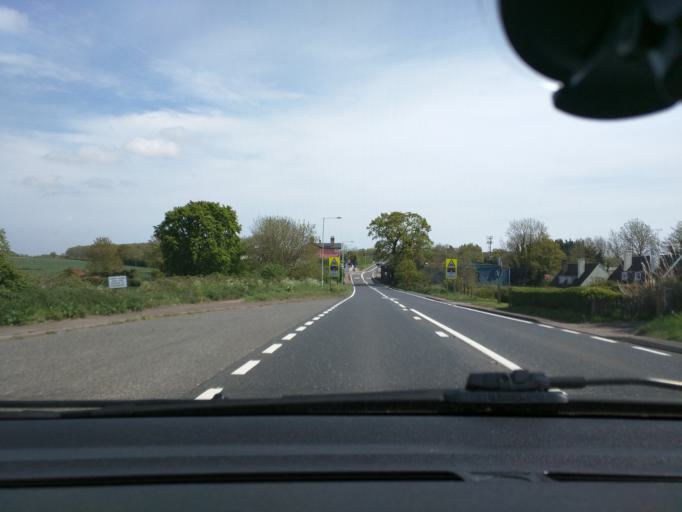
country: GB
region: England
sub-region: Suffolk
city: Saxmundham
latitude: 52.2713
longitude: 1.5214
